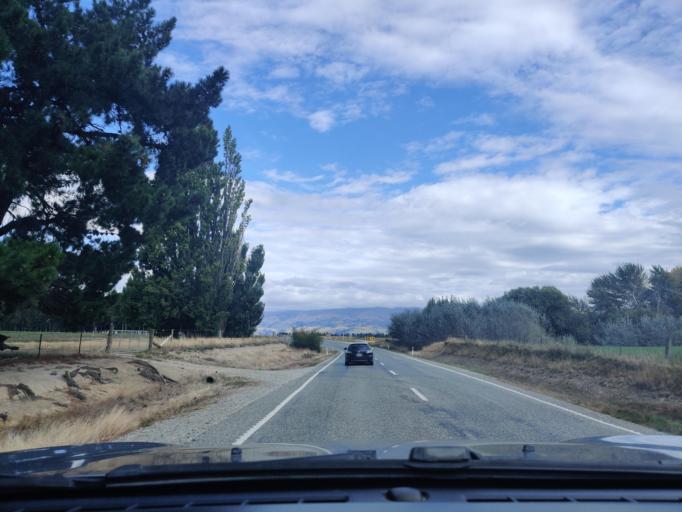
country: NZ
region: Otago
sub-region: Queenstown-Lakes District
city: Wanaka
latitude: -44.8069
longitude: 169.4522
